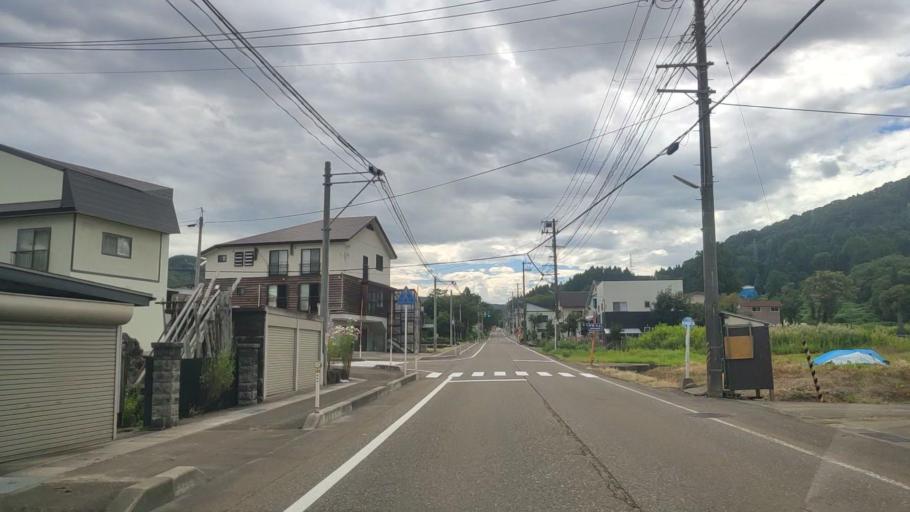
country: JP
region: Niigata
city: Arai
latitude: 37.0021
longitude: 138.2642
